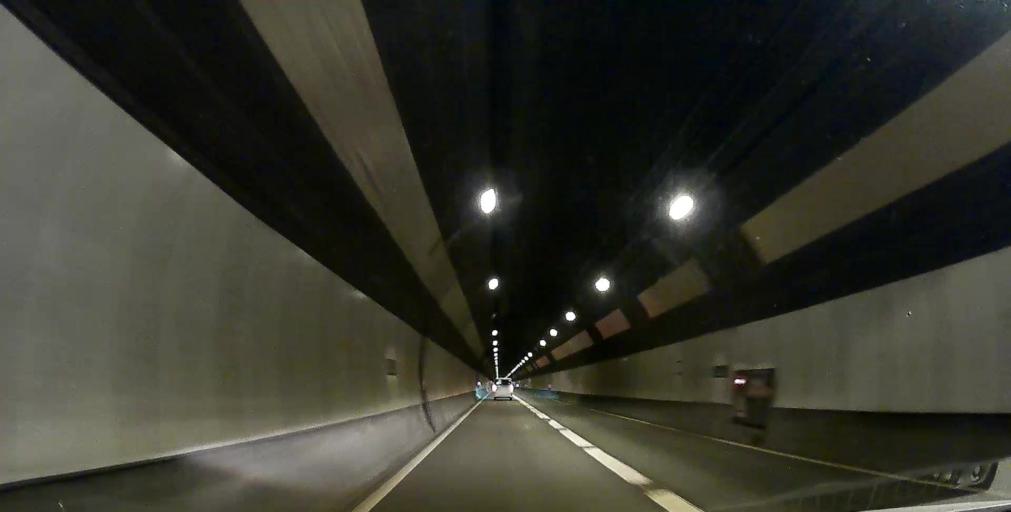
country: JP
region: Yamanashi
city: Enzan
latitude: 35.6251
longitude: 138.7966
